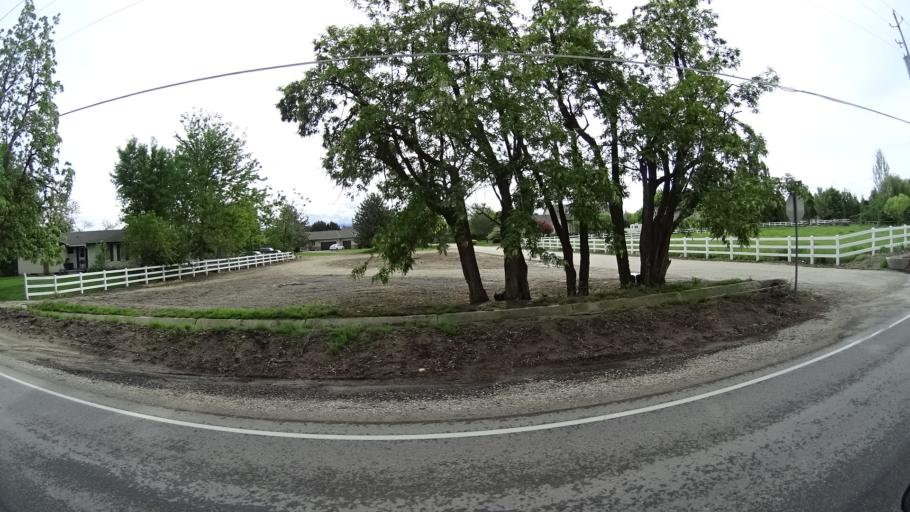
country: US
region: Idaho
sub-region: Ada County
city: Eagle
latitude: 43.7096
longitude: -116.3791
